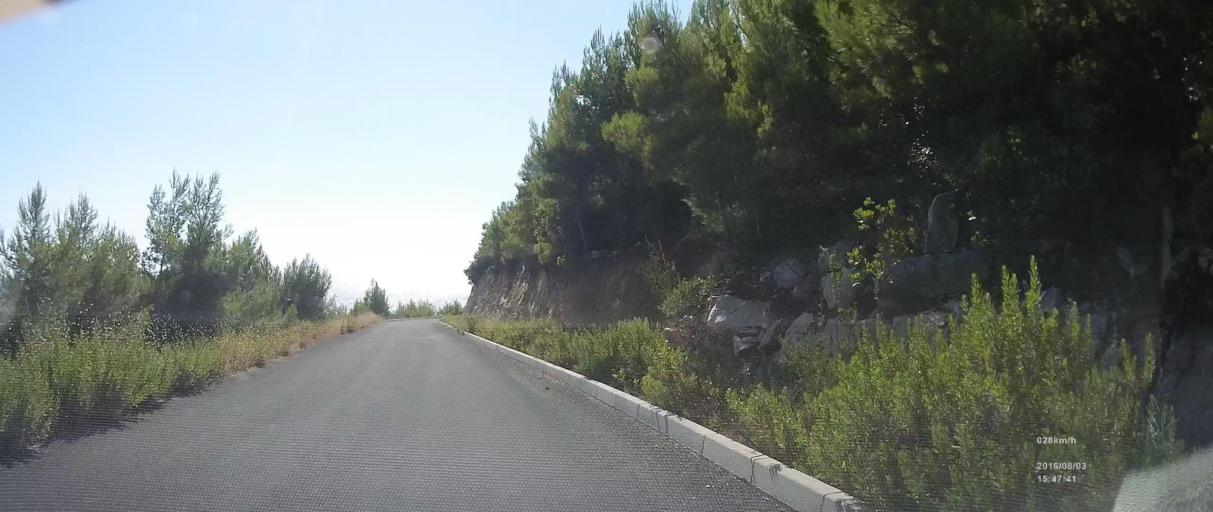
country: HR
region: Dubrovacko-Neretvanska
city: Blato
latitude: 42.7356
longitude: 17.5073
